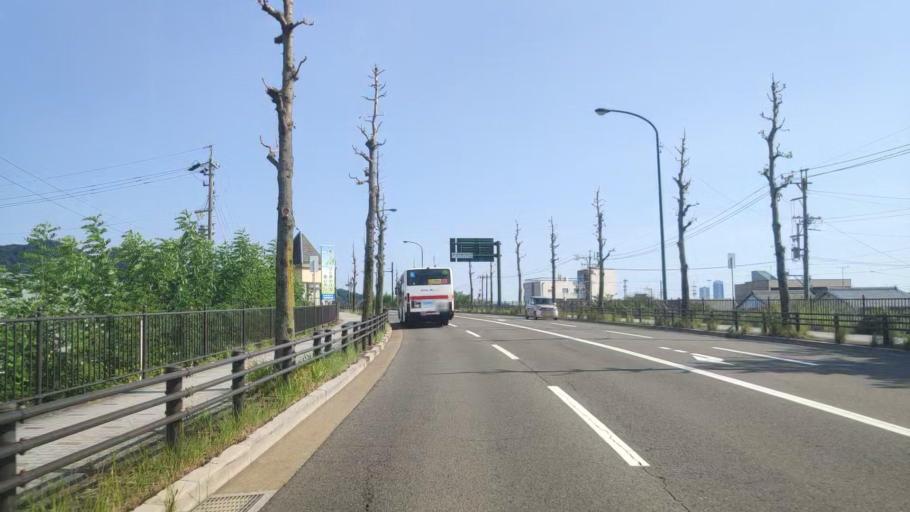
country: JP
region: Gifu
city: Gifu-shi
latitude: 35.4357
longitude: 136.7605
